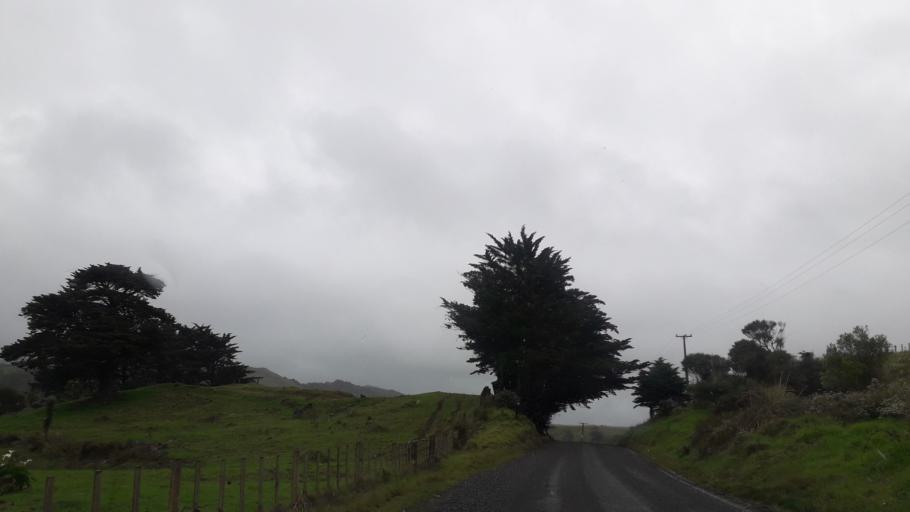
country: NZ
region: Northland
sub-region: Far North District
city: Ahipara
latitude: -35.4188
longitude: 173.3623
